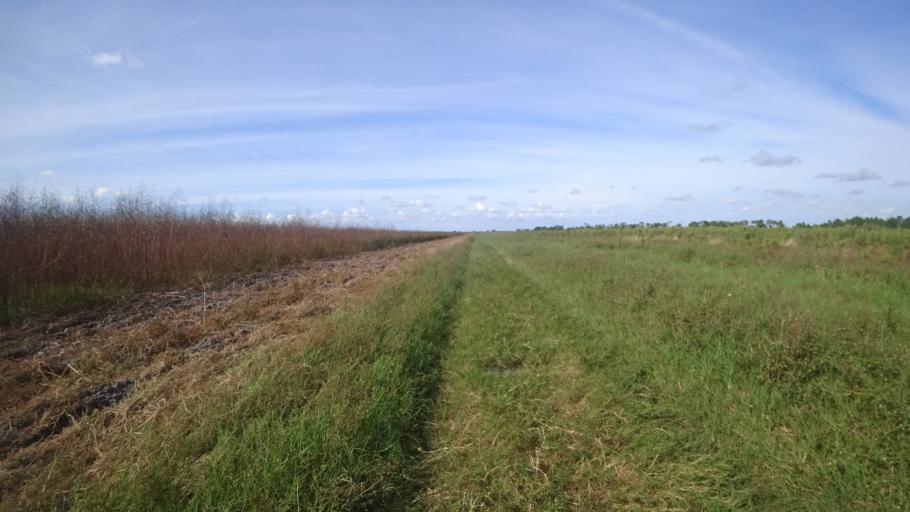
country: US
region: Florida
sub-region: Sarasota County
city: The Meadows
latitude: 27.4521
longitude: -82.3254
